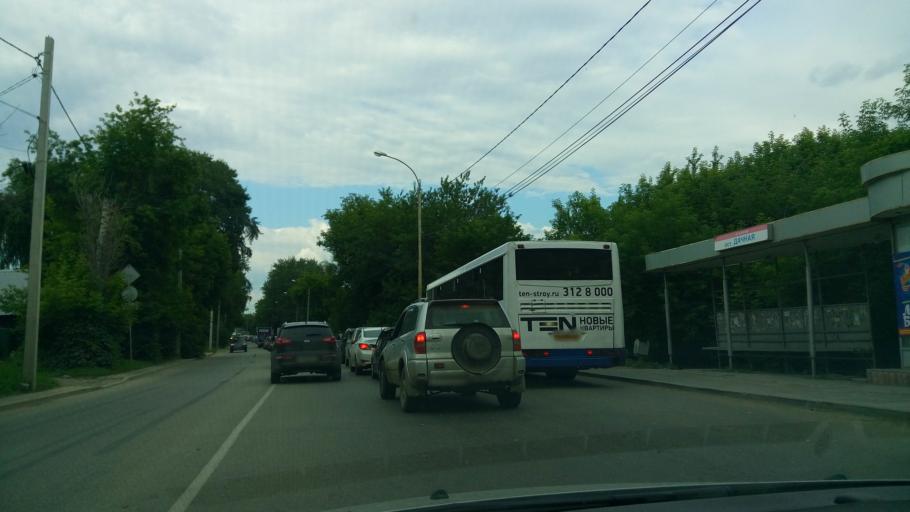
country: RU
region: Sverdlovsk
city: Yekaterinburg
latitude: 56.8724
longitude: 60.6857
